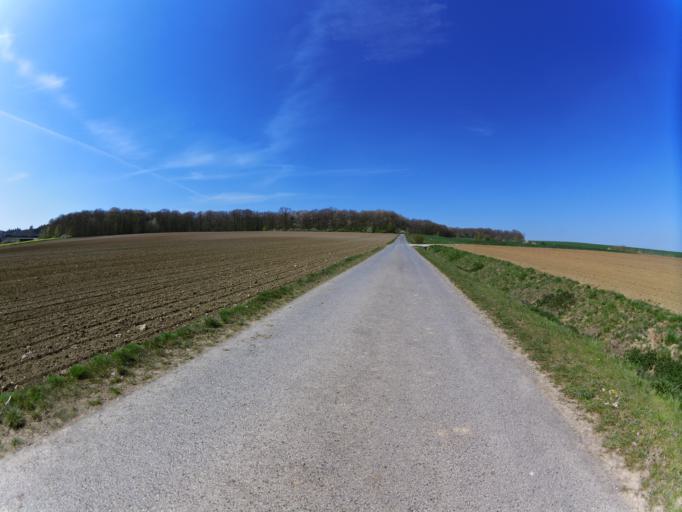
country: DE
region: Bavaria
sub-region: Regierungsbezirk Unterfranken
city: Estenfeld
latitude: 49.8611
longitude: 10.0005
